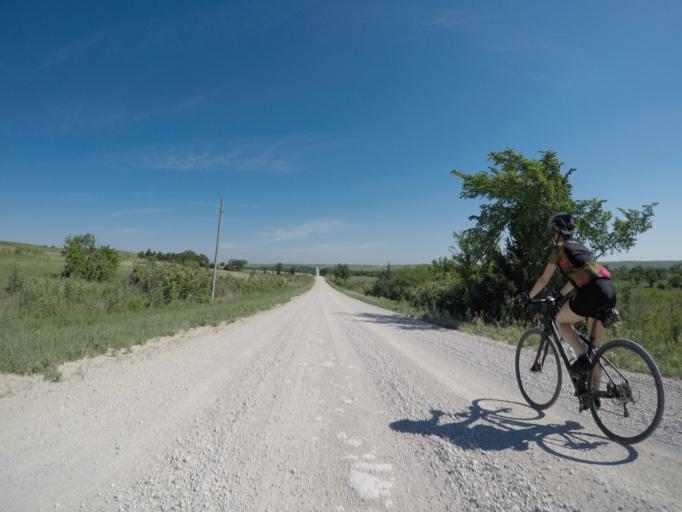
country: US
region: Kansas
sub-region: Wabaunsee County
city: Alma
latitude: 38.9842
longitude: -96.1139
